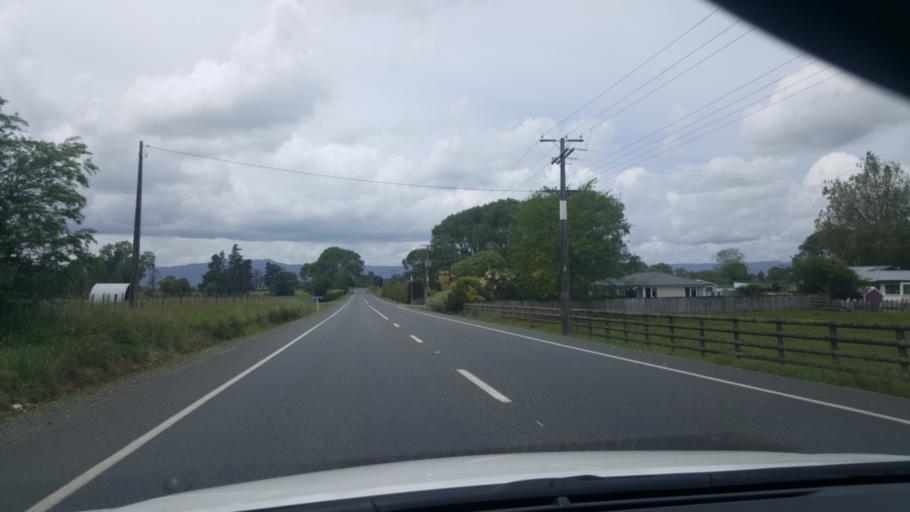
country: NZ
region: Waikato
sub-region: Matamata-Piako District
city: Matamata
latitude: -37.8810
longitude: 175.7447
